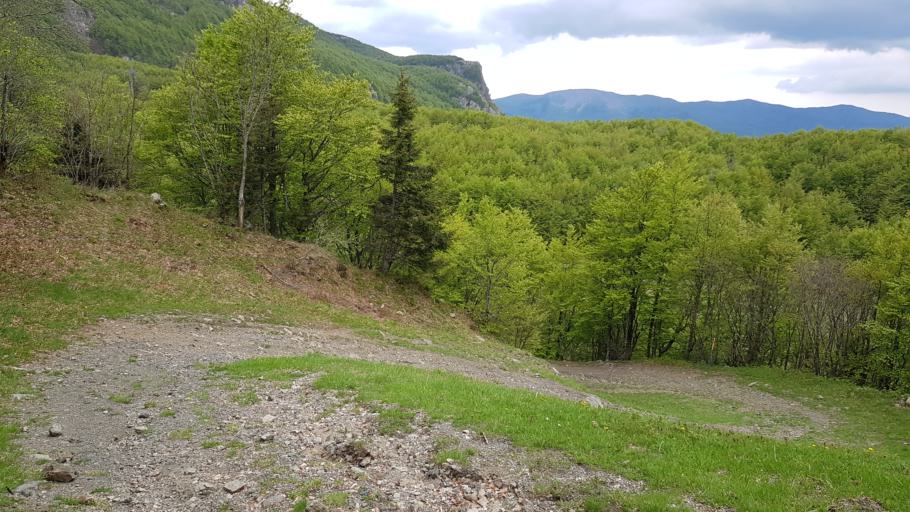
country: IT
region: Liguria
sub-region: Provincia di Genova
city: Santo Stefano d'Aveto
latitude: 44.5595
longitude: 9.4864
